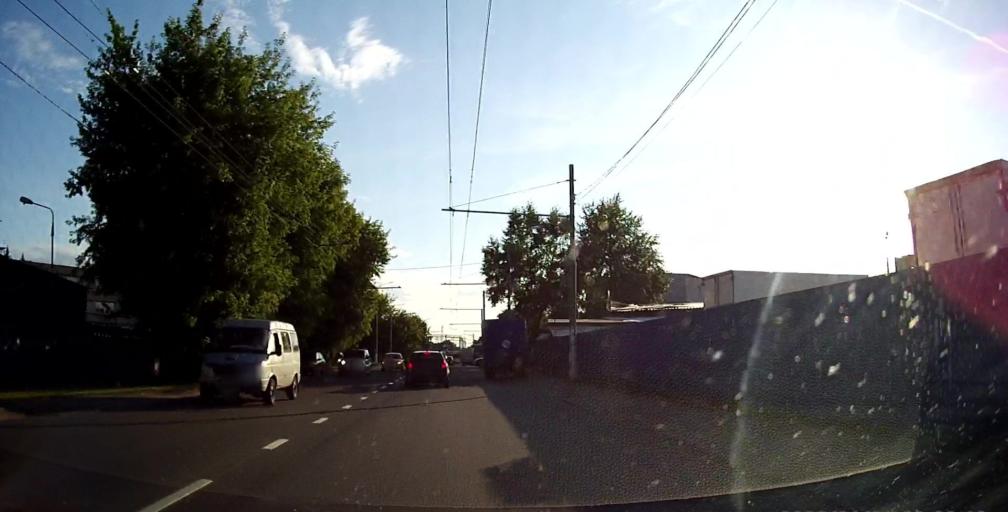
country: RU
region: Moskovskaya
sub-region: Podol'skiy Rayon
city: Podol'sk
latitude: 55.4332
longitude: 37.5705
